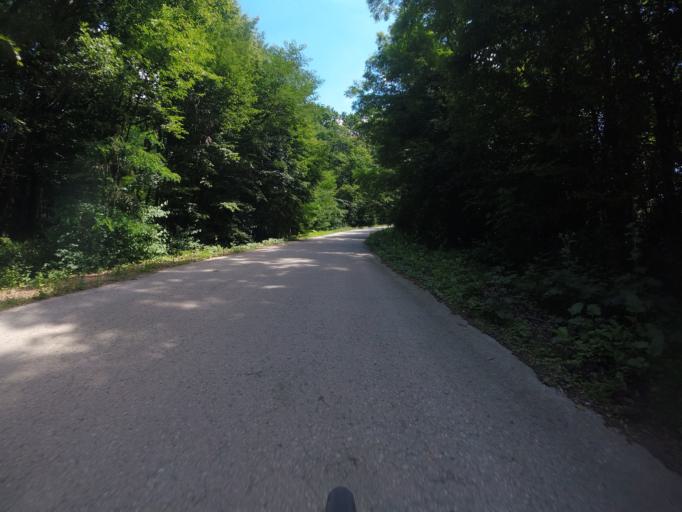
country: HR
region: Karlovacka
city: Ozalj
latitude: 45.6706
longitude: 15.4203
